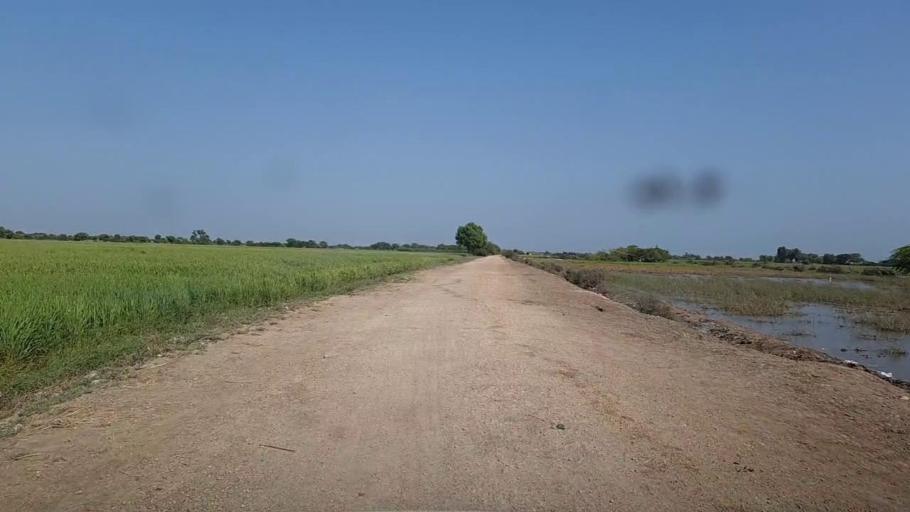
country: PK
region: Sindh
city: Kario
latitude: 24.7518
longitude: 68.4585
